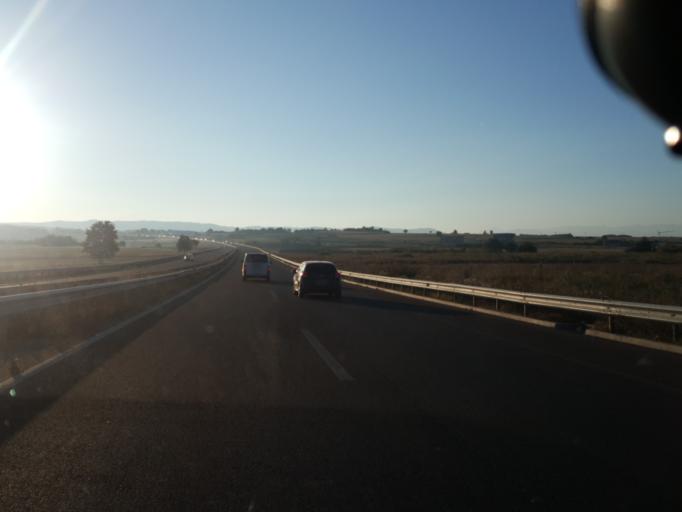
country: XK
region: Prizren
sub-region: Komuna e Malisheves
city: Llazice
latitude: 42.5725
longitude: 20.7293
